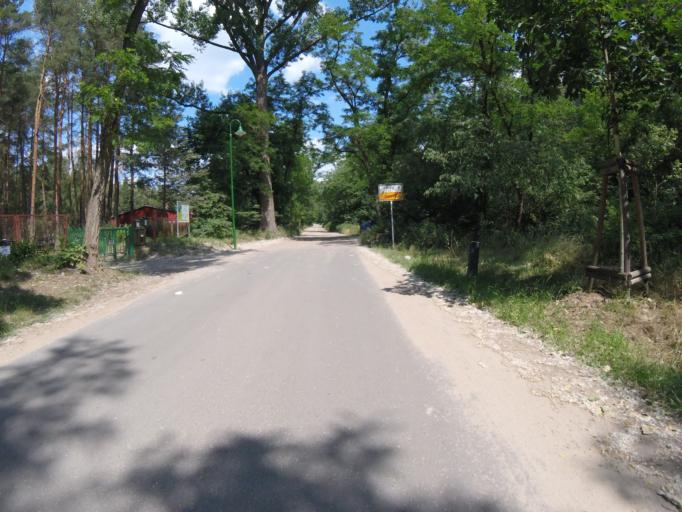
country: DE
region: Brandenburg
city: Bestensee
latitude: 52.2648
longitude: 13.6573
